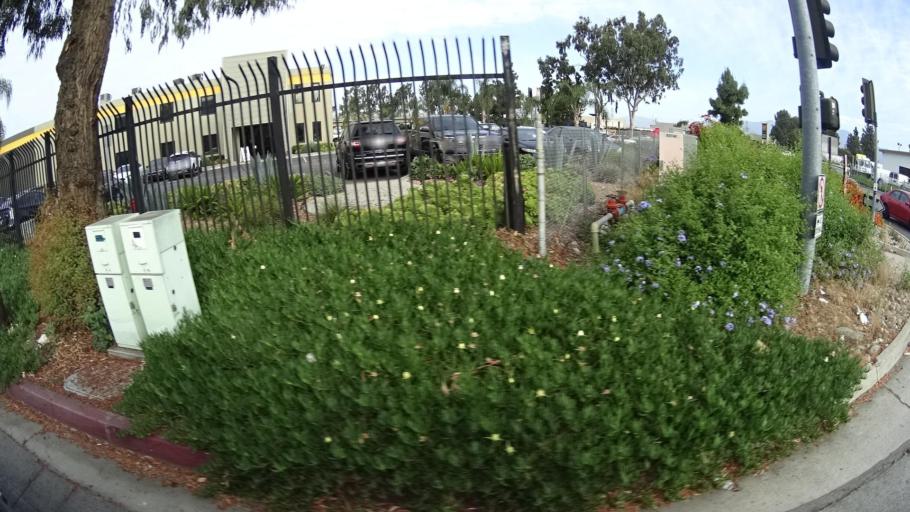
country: US
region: California
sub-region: Los Angeles County
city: South El Monte
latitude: 34.0270
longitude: -118.0358
